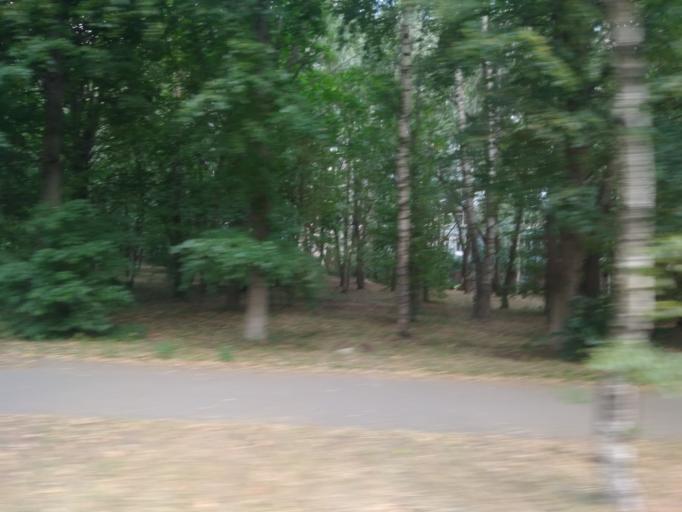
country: RU
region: Moskovskaya
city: Bykovo
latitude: 55.6022
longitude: 38.0898
